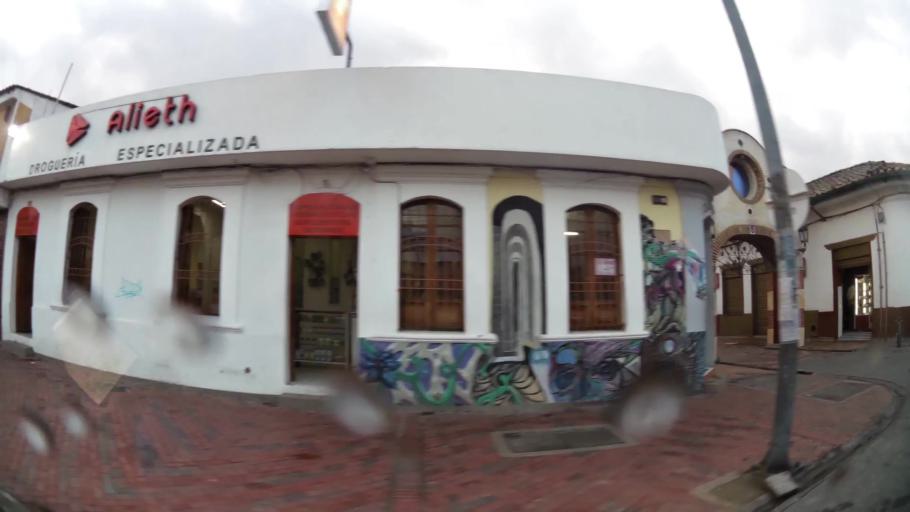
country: CO
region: Cundinamarca
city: Chia
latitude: 4.8610
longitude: -74.0589
